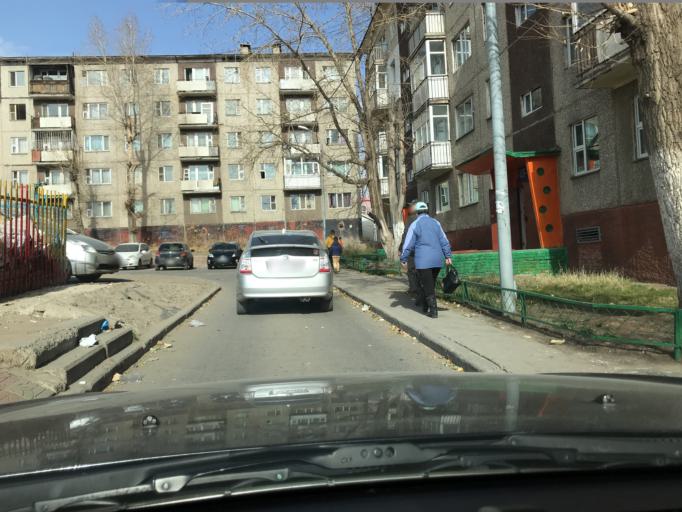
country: MN
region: Ulaanbaatar
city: Ulaanbaatar
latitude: 47.9205
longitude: 106.9520
